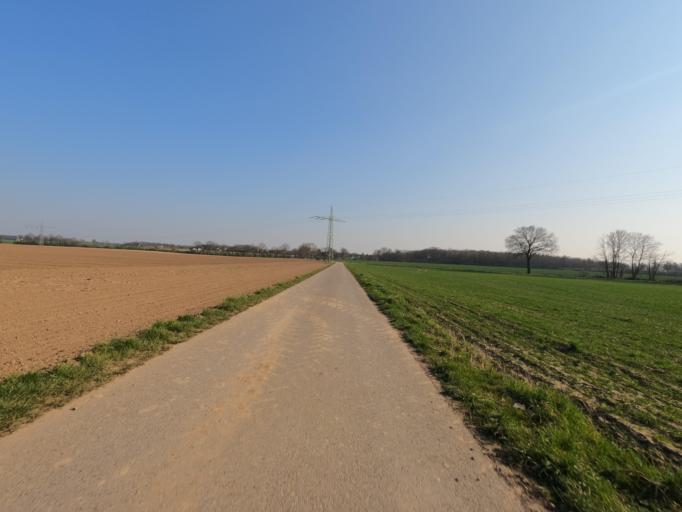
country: DE
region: North Rhine-Westphalia
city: Huckelhoven
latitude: 51.0650
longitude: 6.2640
